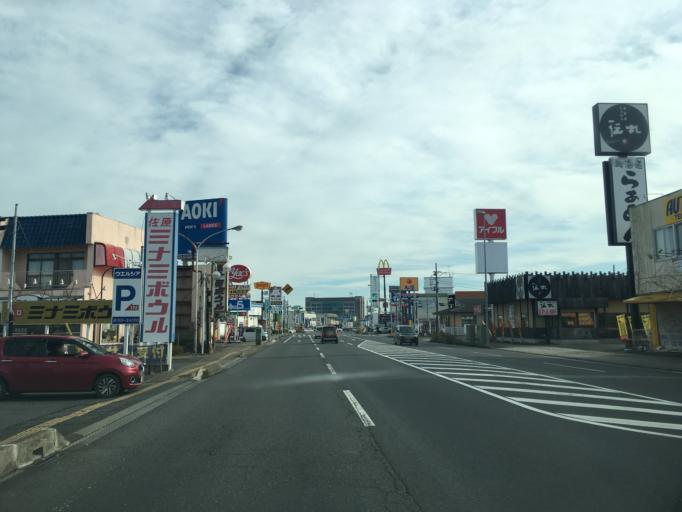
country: JP
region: Chiba
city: Katori-shi
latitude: 35.9002
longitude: 140.4928
